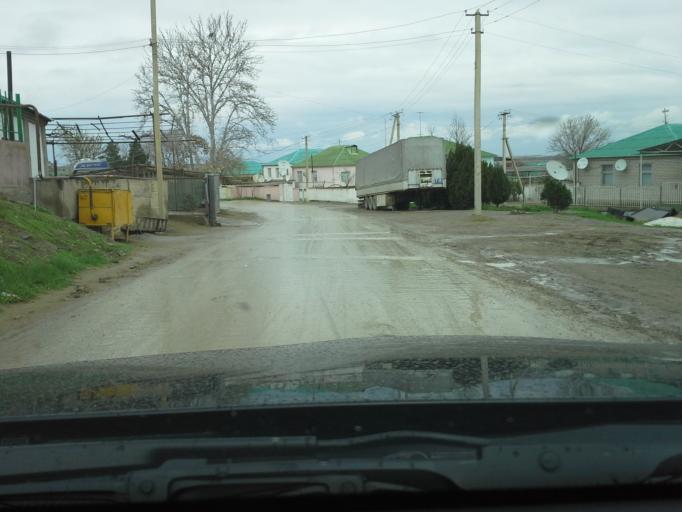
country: TM
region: Ahal
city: Abadan
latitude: 37.9625
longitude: 58.2111
